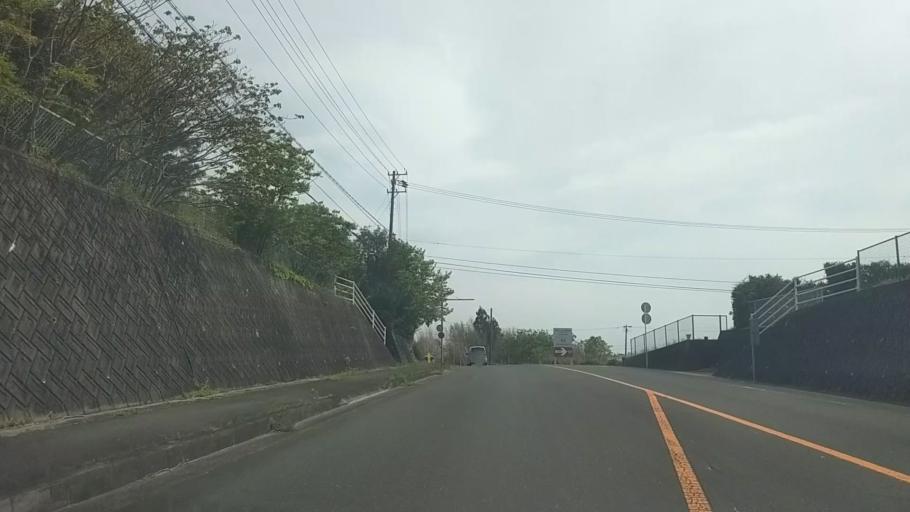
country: JP
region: Shizuoka
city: Kosai-shi
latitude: 34.7796
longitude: 137.6379
